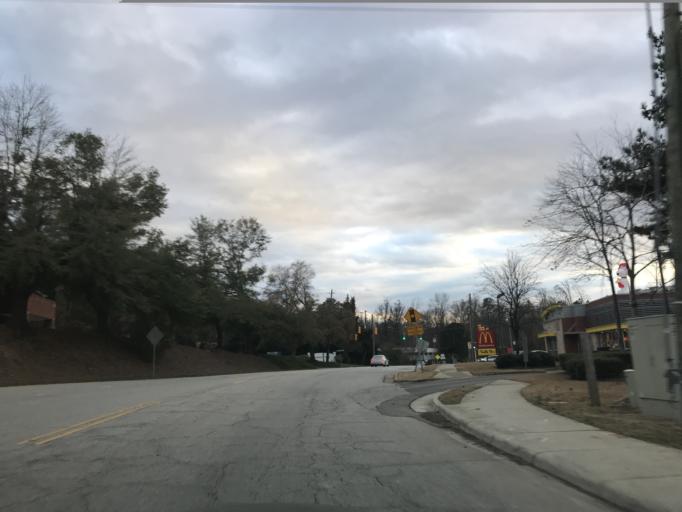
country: US
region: North Carolina
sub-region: Wake County
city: West Raleigh
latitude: 35.8364
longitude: -78.6750
